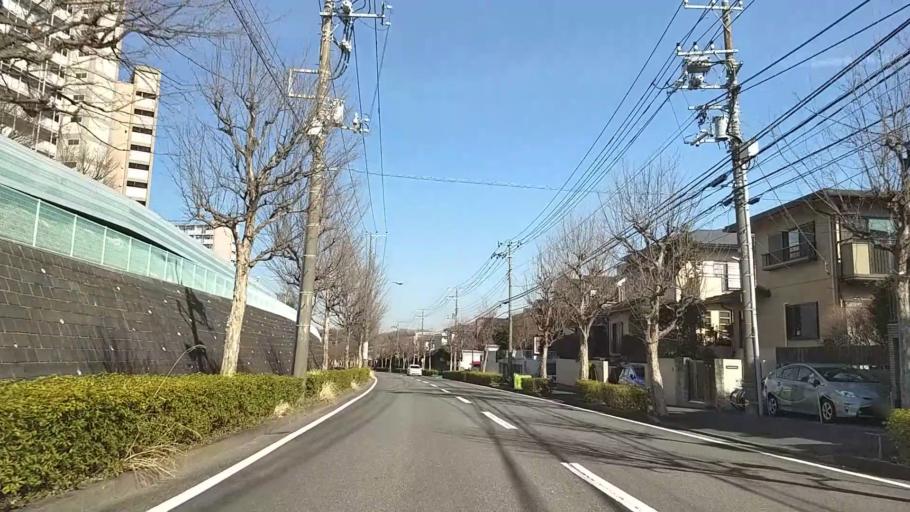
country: JP
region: Kanagawa
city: Kamakura
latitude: 35.3763
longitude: 139.5856
